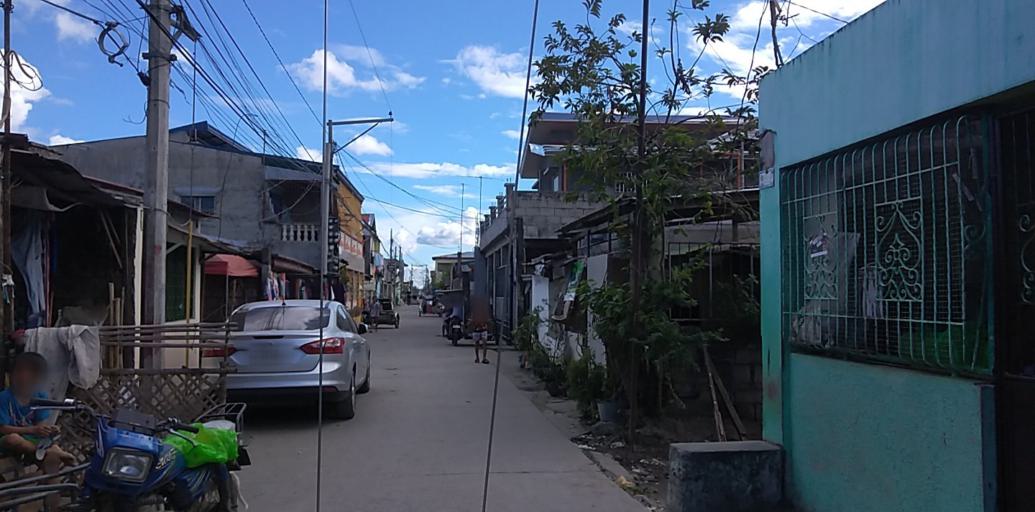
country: PH
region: Central Luzon
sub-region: Province of Pampanga
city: Arayat
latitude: 15.1407
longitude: 120.7693
